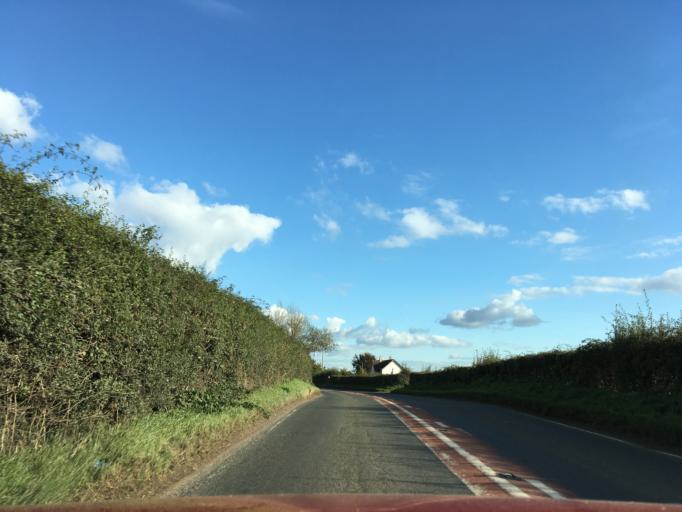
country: GB
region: England
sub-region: Herefordshire
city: Bridge Sollers
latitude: 52.0782
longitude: -2.8511
